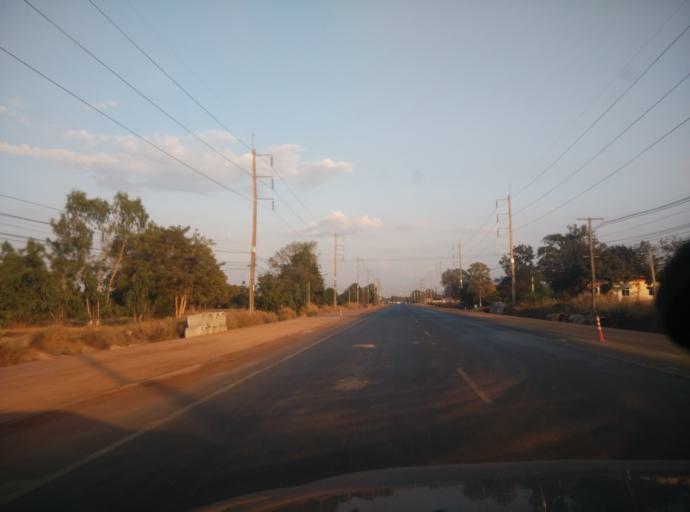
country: TH
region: Sisaket
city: Uthumphon Phisai
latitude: 15.1493
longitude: 104.2177
